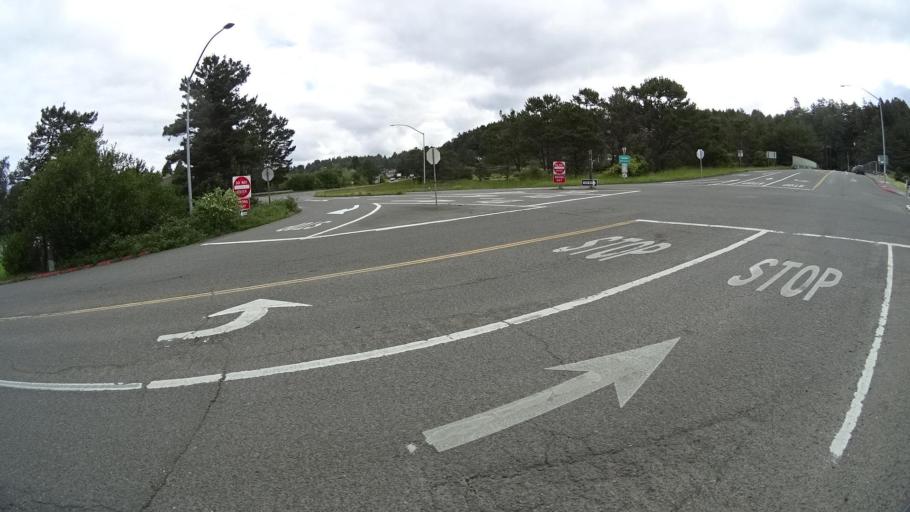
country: US
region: California
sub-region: Humboldt County
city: Arcata
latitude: 40.8787
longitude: -124.0840
